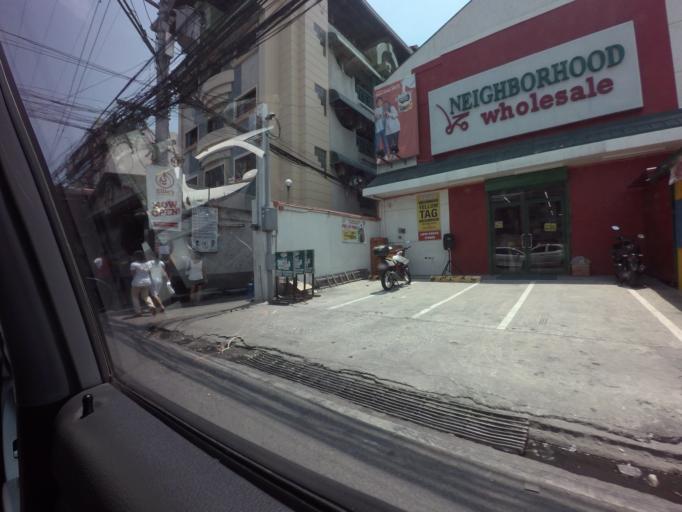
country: PH
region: Metro Manila
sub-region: City of Manila
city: Quiapo
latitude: 14.5839
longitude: 120.9986
